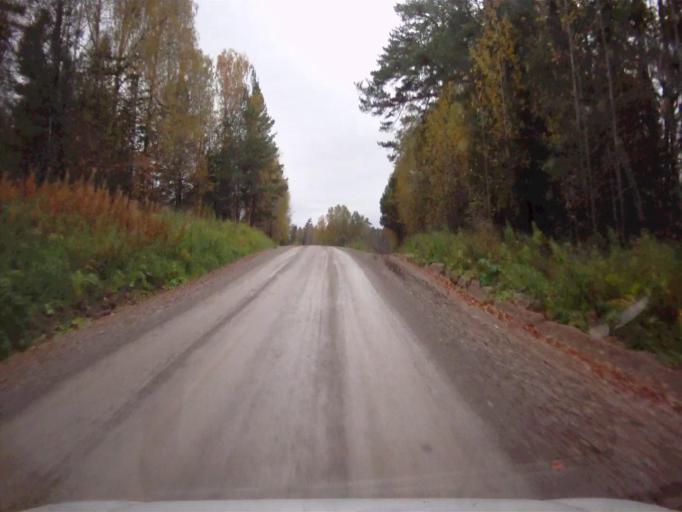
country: RU
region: Chelyabinsk
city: Nyazepetrovsk
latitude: 56.0491
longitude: 59.4985
